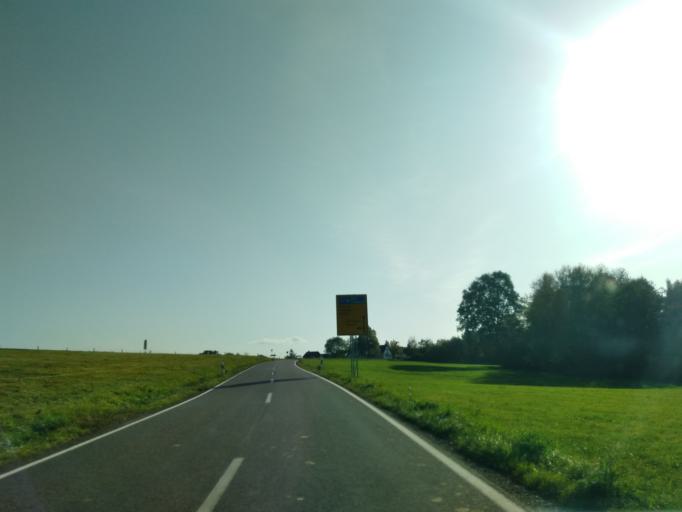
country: DE
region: Rheinland-Pfalz
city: Asbach
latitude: 50.6714
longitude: 7.4339
